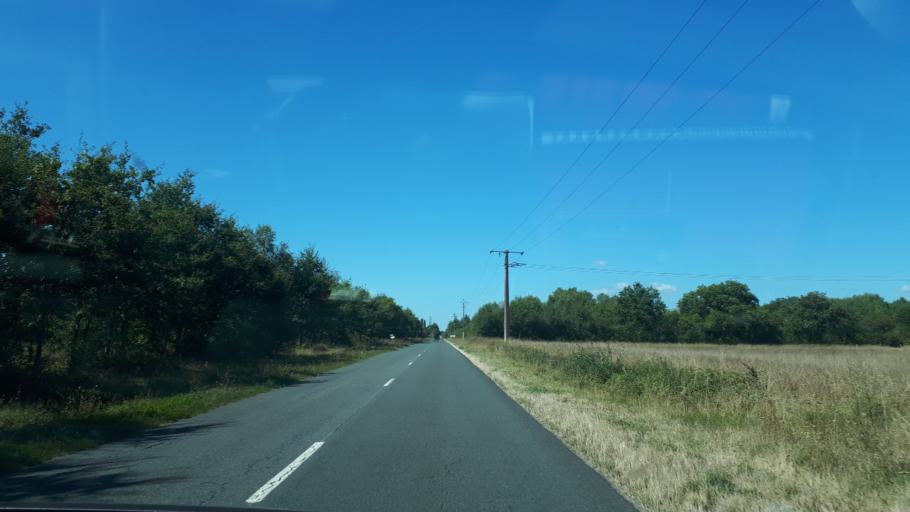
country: FR
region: Centre
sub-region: Departement du Cher
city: Brinon-sur-Sauldre
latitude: 47.6498
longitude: 2.1830
